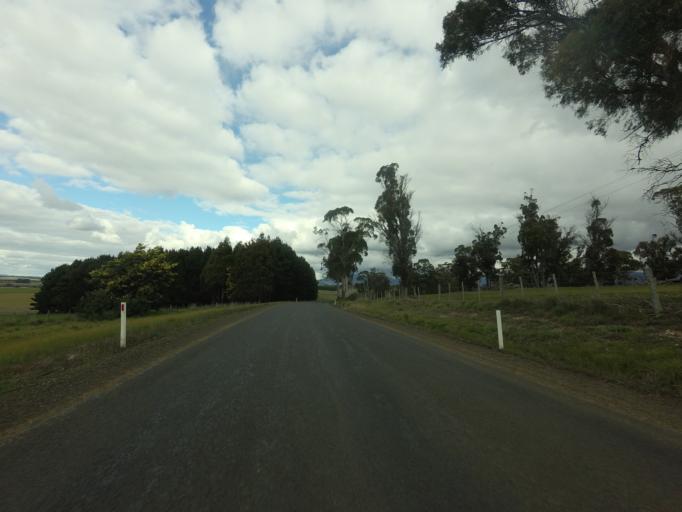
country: AU
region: Tasmania
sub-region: Northern Midlands
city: Longford
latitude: -41.7668
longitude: 147.0857
